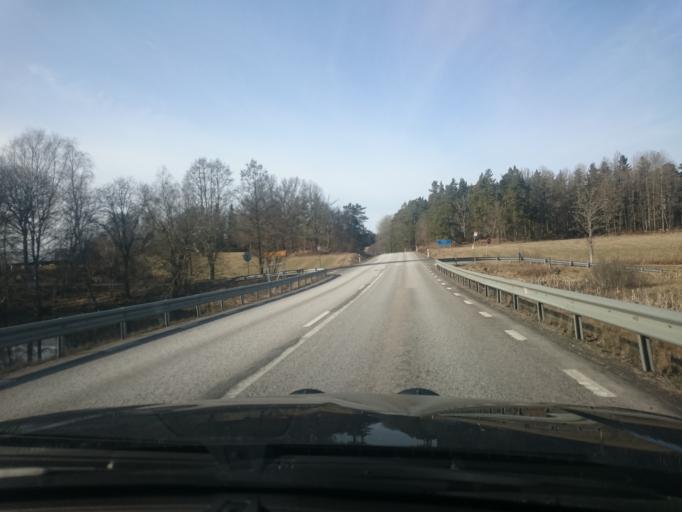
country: SE
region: Joenkoeping
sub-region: Vetlanda Kommun
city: Vetlanda
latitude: 57.3182
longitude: 15.1185
